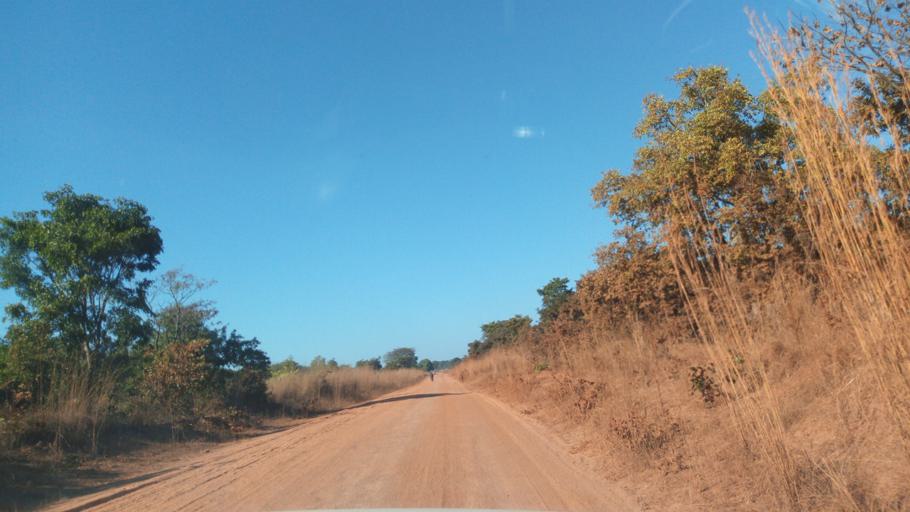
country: ZM
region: Luapula
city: Mwense
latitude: -10.6173
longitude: 28.4123
